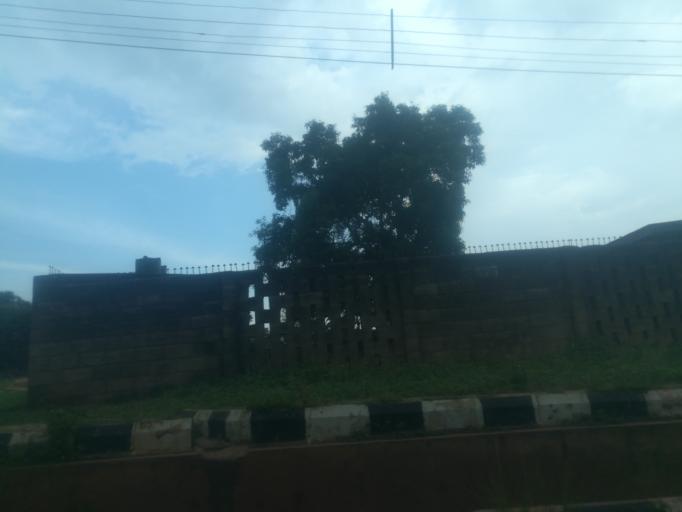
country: NG
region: Oyo
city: Ibadan
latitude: 7.4309
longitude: 3.8930
